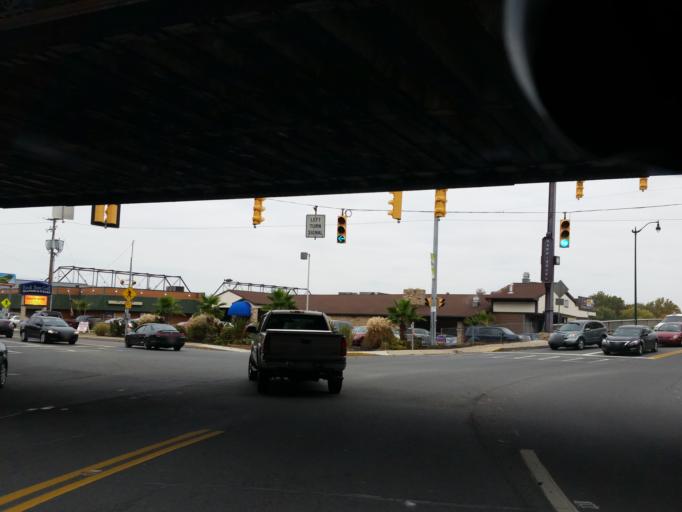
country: US
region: Pennsylvania
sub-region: Cumberland County
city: Lemoyne
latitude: 40.2496
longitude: -76.8914
